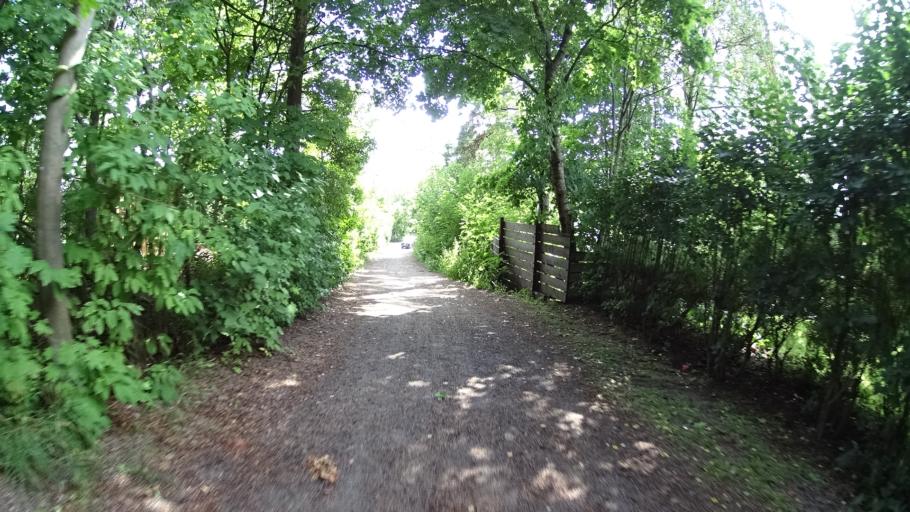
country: FI
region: Uusimaa
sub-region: Helsinki
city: Kilo
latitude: 60.2010
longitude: 24.7684
